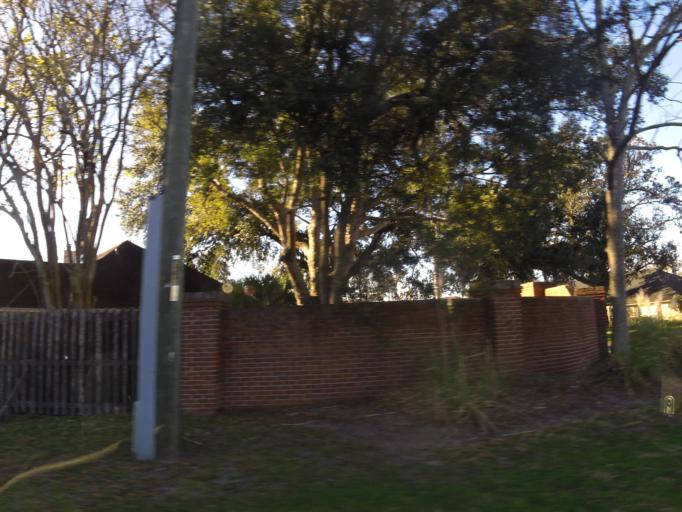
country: US
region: Florida
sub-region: Saint Johns County
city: Fruit Cove
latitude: 30.2103
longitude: -81.6054
